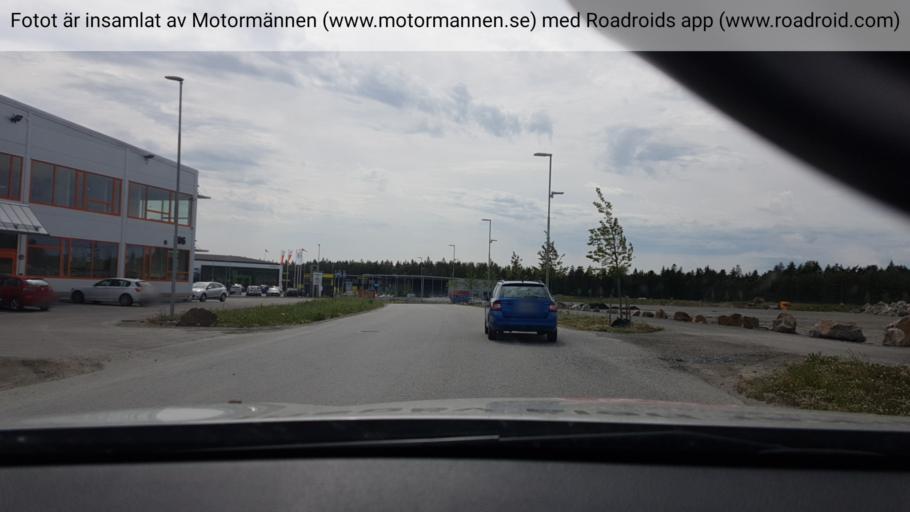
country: SE
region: Stockholm
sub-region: Haninge Kommun
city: Haninge
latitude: 59.1533
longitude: 18.1618
